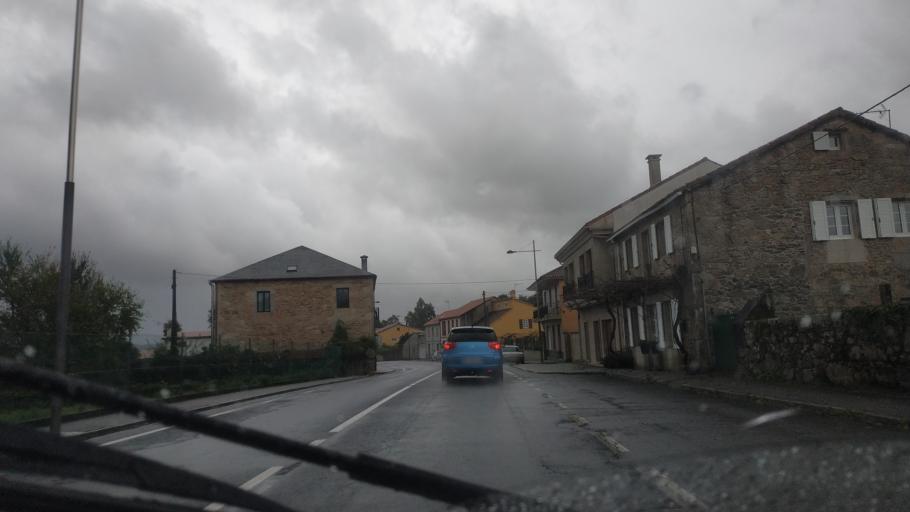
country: ES
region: Galicia
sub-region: Provincia da Coruna
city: Negreira
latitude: 42.9228
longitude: -8.7342
